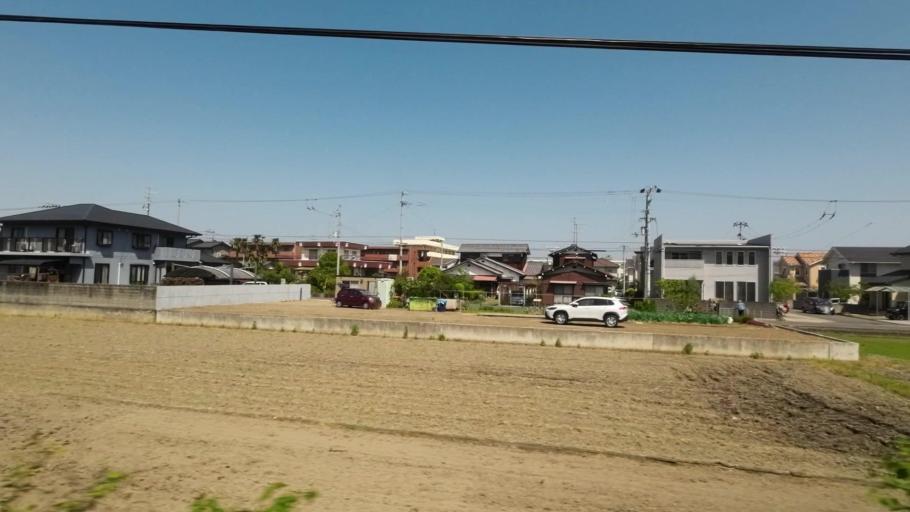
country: JP
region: Ehime
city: Niihama
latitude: 33.9658
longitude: 133.3168
